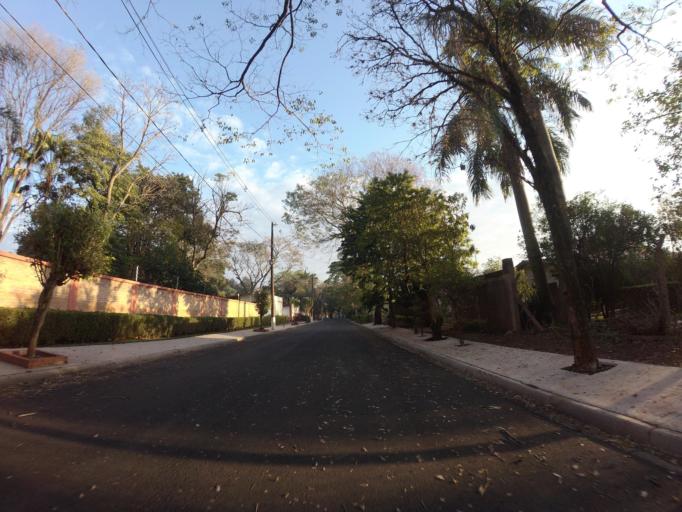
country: BR
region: Sao Paulo
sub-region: Piracicaba
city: Piracicaba
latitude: -22.7558
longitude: -47.5910
